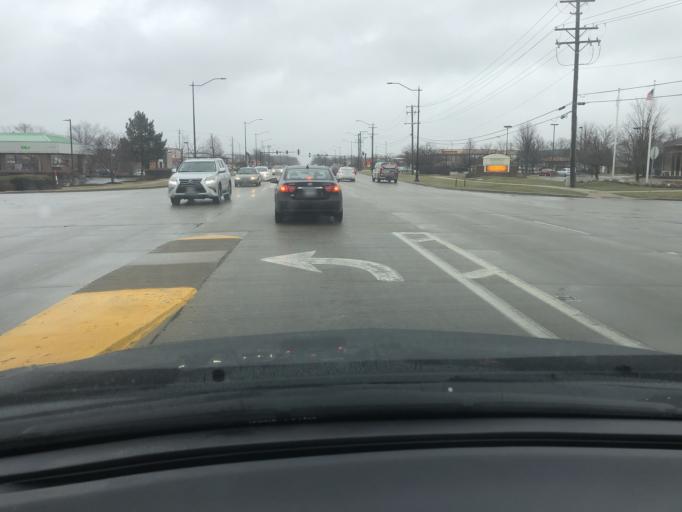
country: US
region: Illinois
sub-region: Will County
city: Shorewood
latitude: 41.5382
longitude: -88.1993
